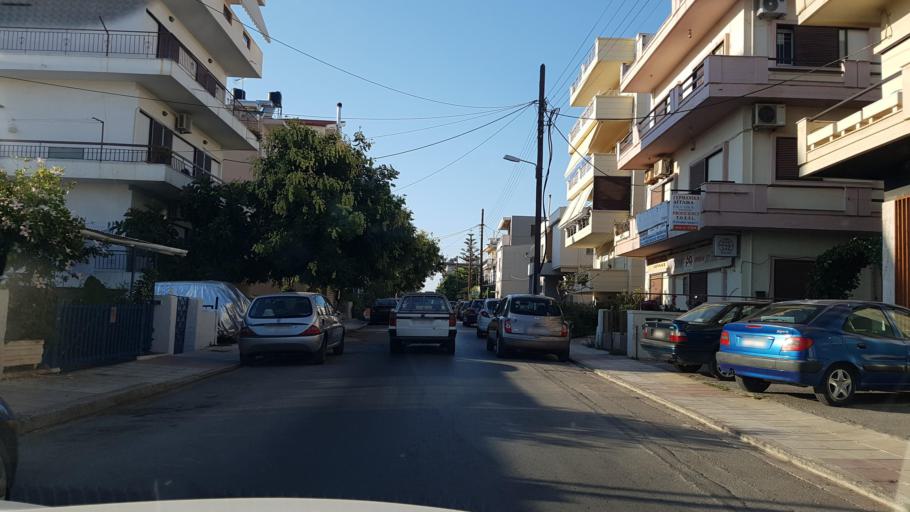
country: GR
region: Crete
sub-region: Nomos Chanias
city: Chania
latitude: 35.5084
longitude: 24.0141
